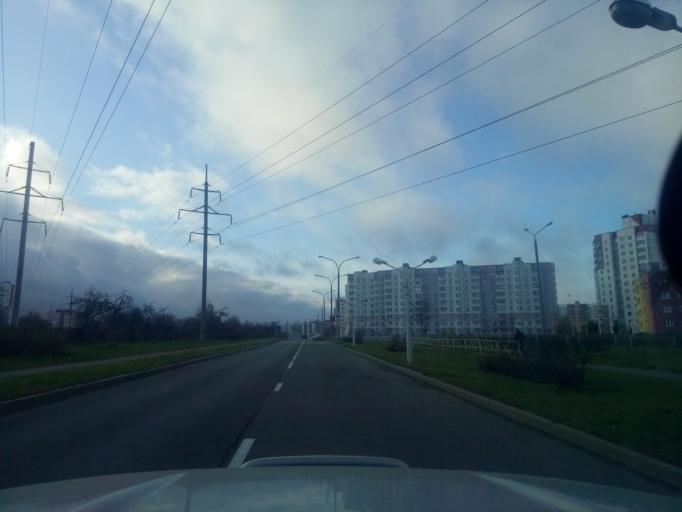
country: BY
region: Minsk
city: Novoye Medvezhino
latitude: 53.8762
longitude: 27.4891
